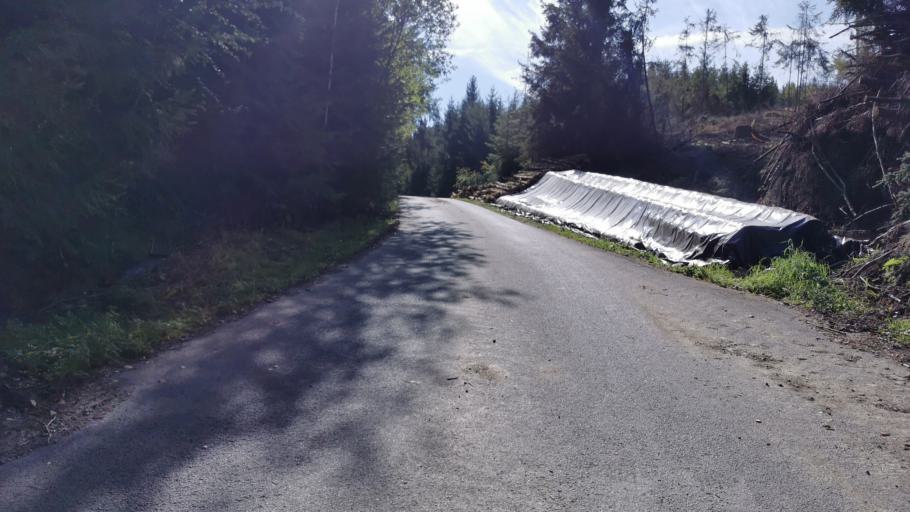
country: DE
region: Bavaria
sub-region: Upper Franconia
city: Ludwigsstadt
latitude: 50.4798
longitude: 11.4164
